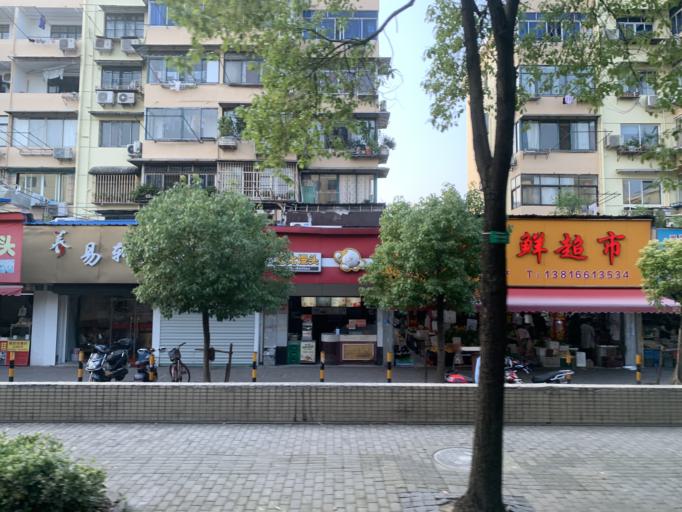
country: CN
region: Shanghai Shi
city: Huamu
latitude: 31.1869
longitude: 121.5391
